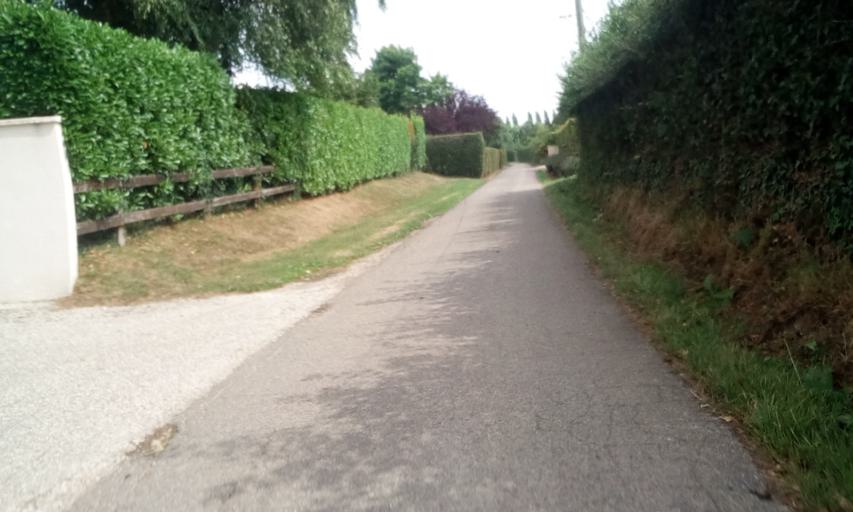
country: FR
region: Lower Normandy
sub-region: Departement du Calvados
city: Bavent
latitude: 49.2498
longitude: -0.1929
